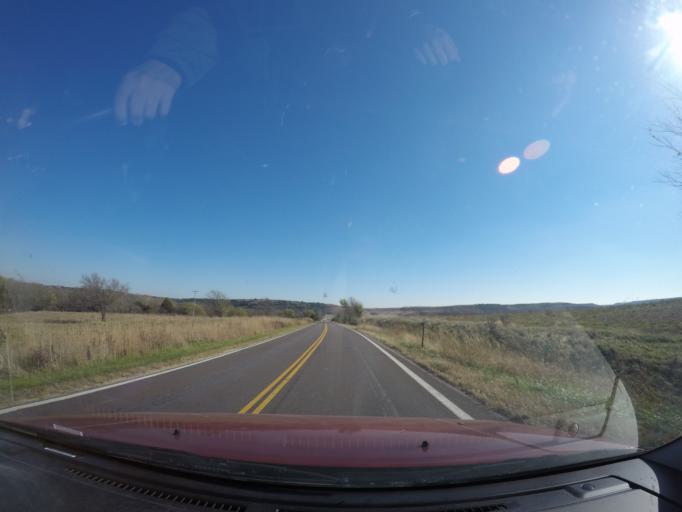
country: US
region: Kansas
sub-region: Geary County
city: Grandview Plaza
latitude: 39.0080
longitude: -96.7462
